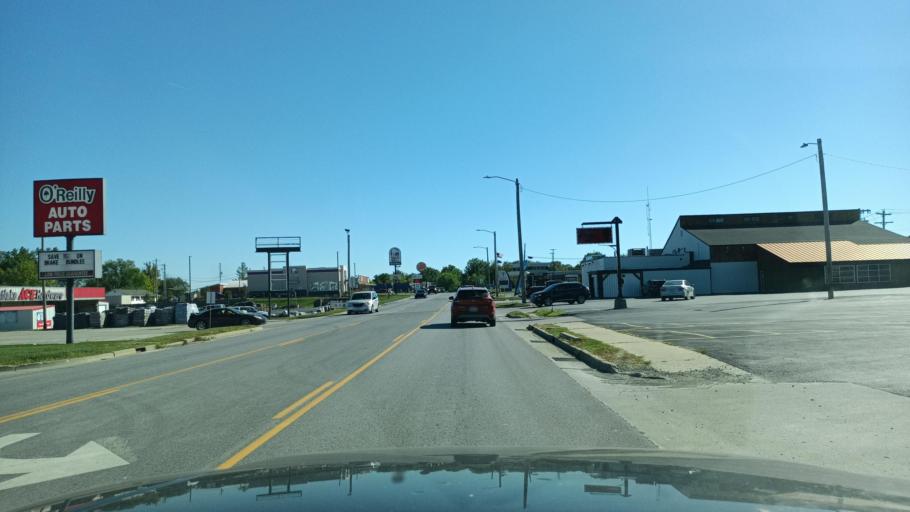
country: US
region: Missouri
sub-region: Macon County
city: Macon
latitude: 39.7502
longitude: -92.4680
